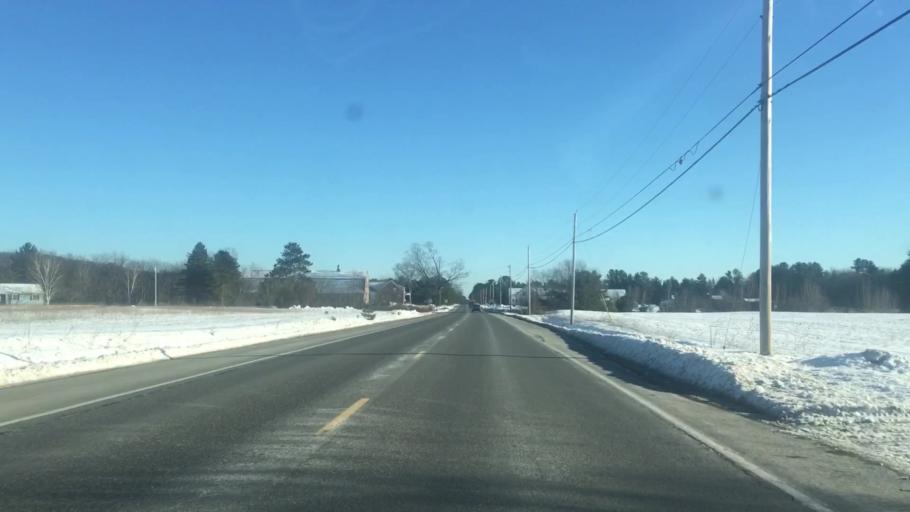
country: US
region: Maine
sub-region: Somerset County
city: Norridgewock
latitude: 44.7092
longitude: -69.7780
